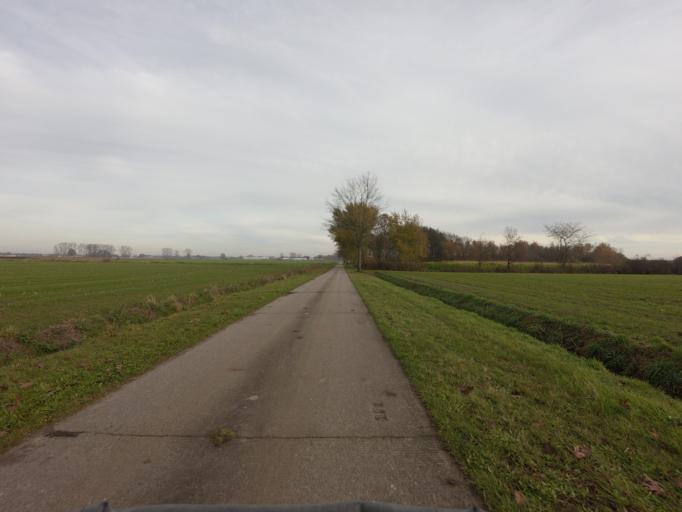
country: BE
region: Flanders
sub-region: Provincie Antwerpen
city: Hoogstraten
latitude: 51.4621
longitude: 4.7699
